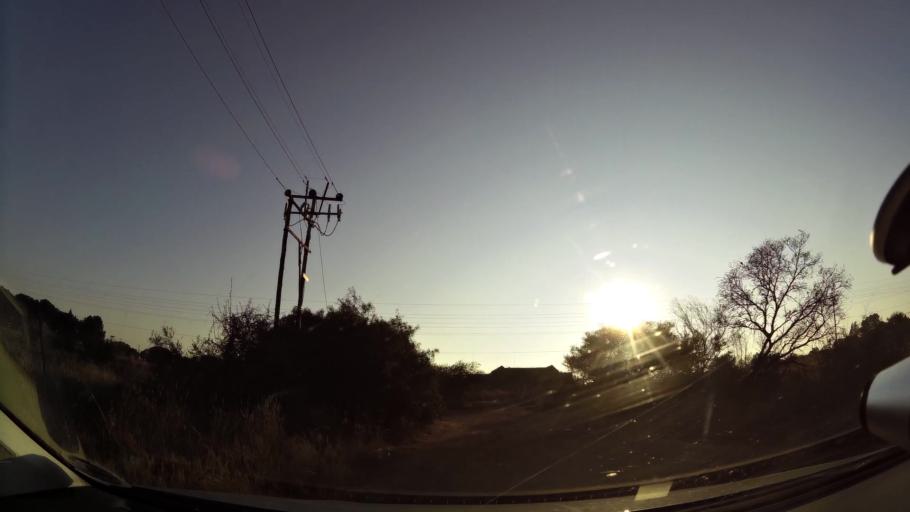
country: ZA
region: Orange Free State
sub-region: Mangaung Metropolitan Municipality
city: Bloemfontein
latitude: -29.0777
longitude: 26.1506
